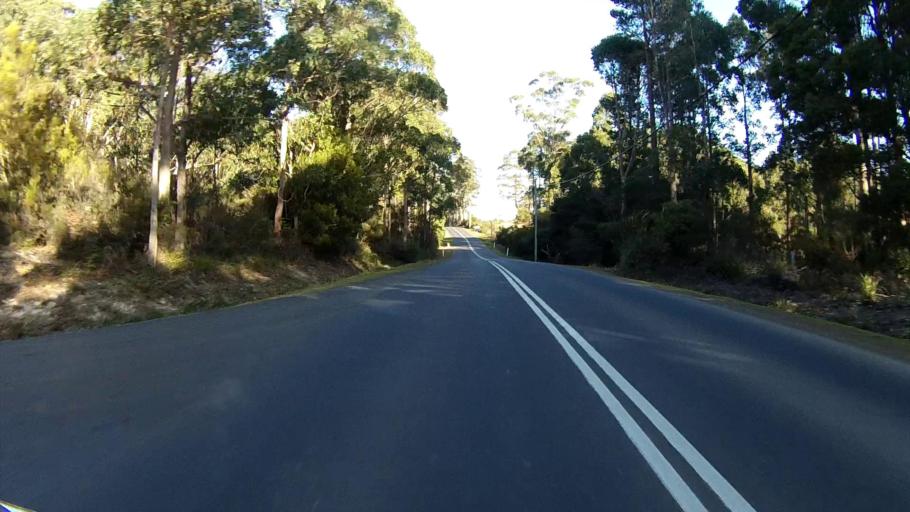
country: AU
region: Tasmania
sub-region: Clarence
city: Sandford
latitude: -43.1306
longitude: 147.8496
